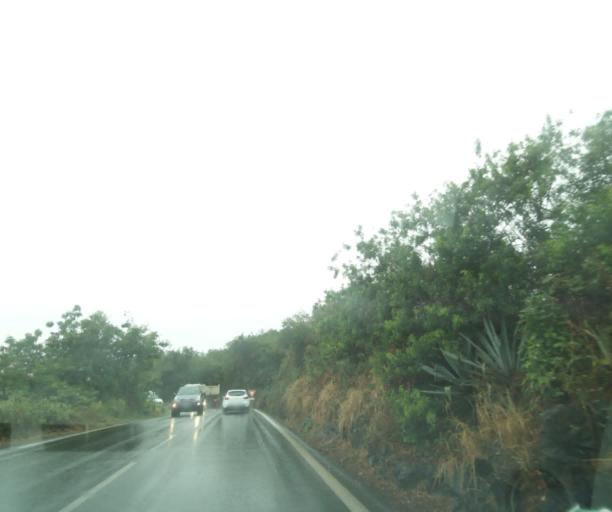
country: RE
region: Reunion
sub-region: Reunion
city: Saint-Paul
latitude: -21.0318
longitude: 55.2836
